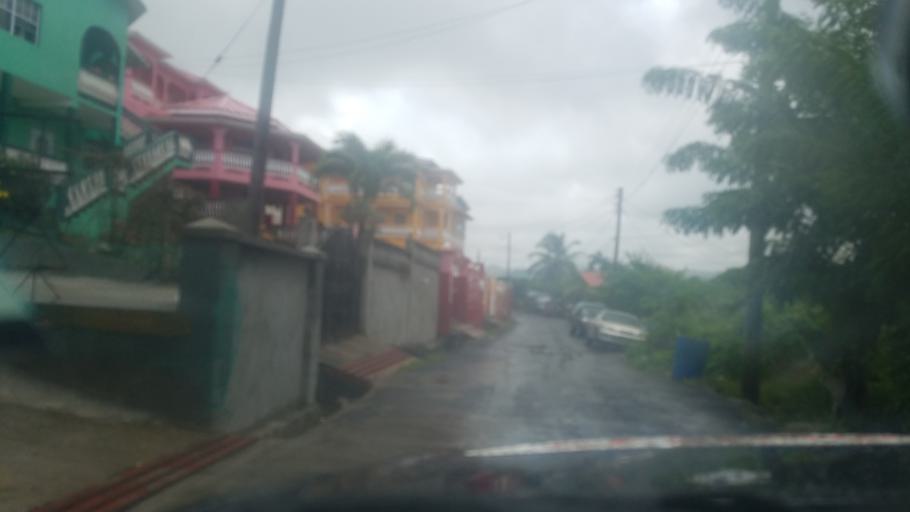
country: LC
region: Laborie Quarter
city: Laborie
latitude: 13.7483
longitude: -60.9679
